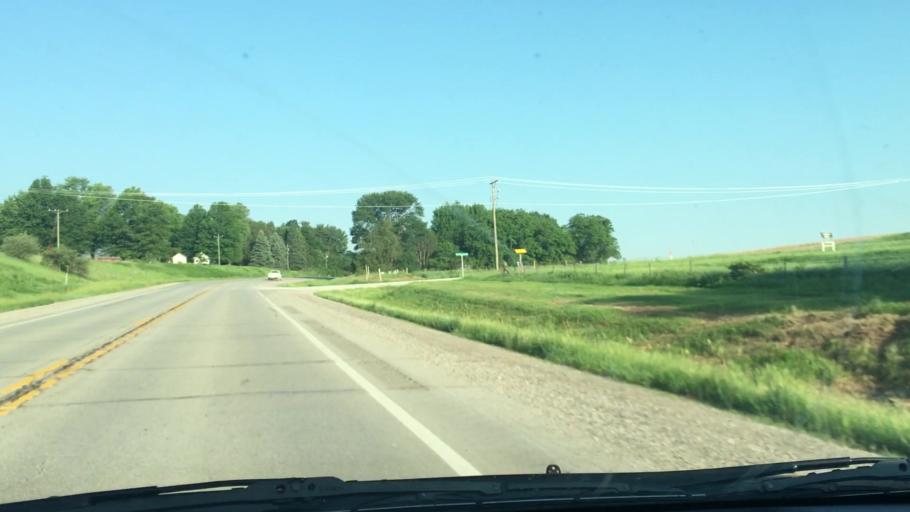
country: US
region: Iowa
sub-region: Johnson County
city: Tiffin
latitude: 41.7090
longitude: -91.6852
